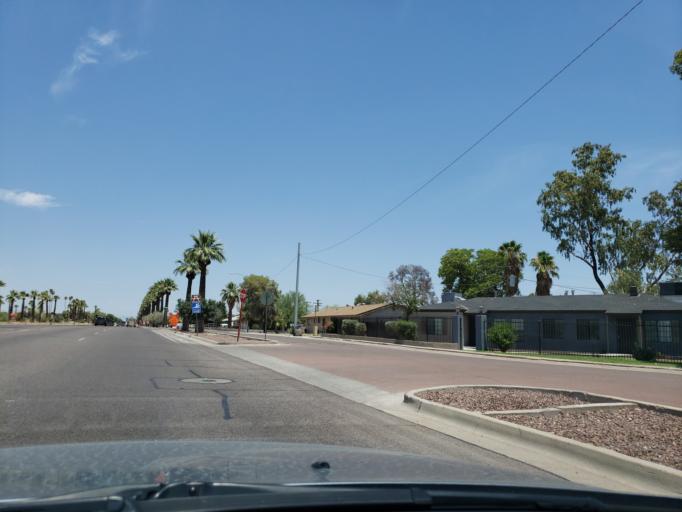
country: US
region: Arizona
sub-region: Maricopa County
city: Goodyear
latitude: 33.4421
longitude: -112.3582
